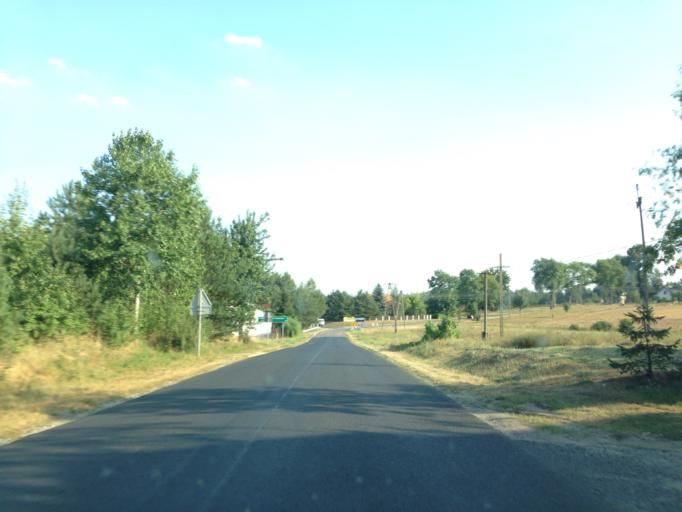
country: PL
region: Warmian-Masurian Voivodeship
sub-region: Powiat nowomiejski
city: Biskupiec
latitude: 53.3867
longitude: 19.3770
